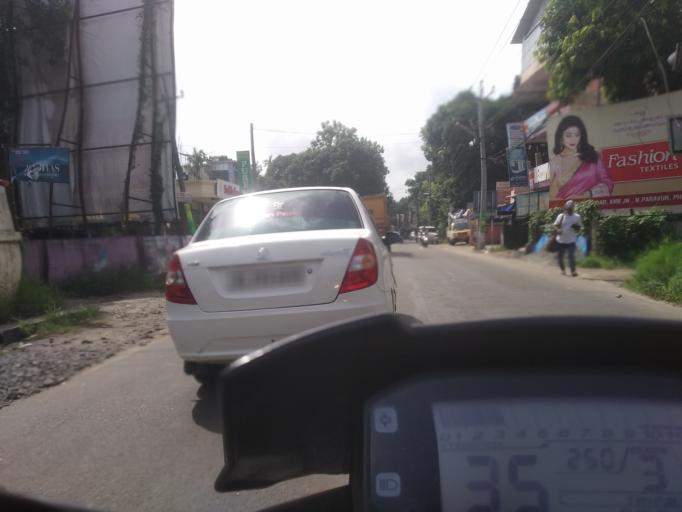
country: IN
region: Kerala
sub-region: Thrissur District
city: Kodungallur
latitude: 10.1411
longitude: 76.2293
